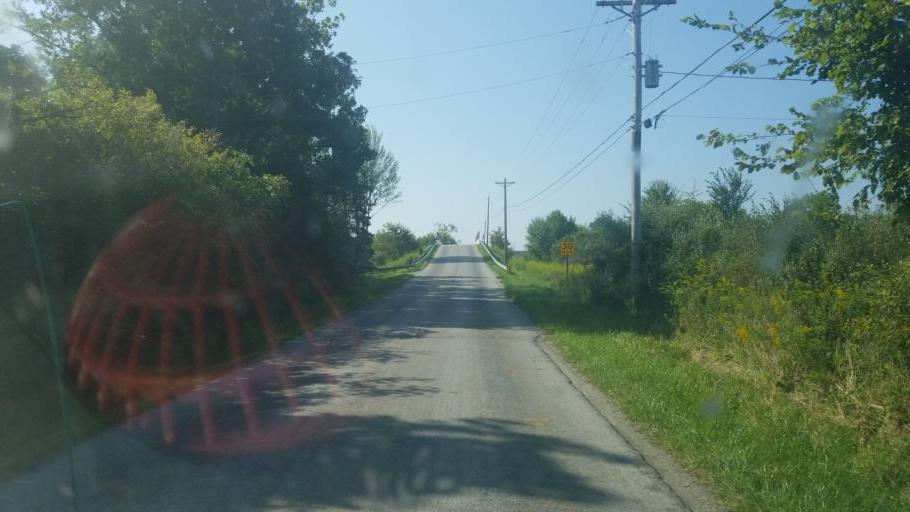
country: US
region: Ohio
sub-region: Wayne County
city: West Salem
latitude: 41.0418
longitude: -82.2017
